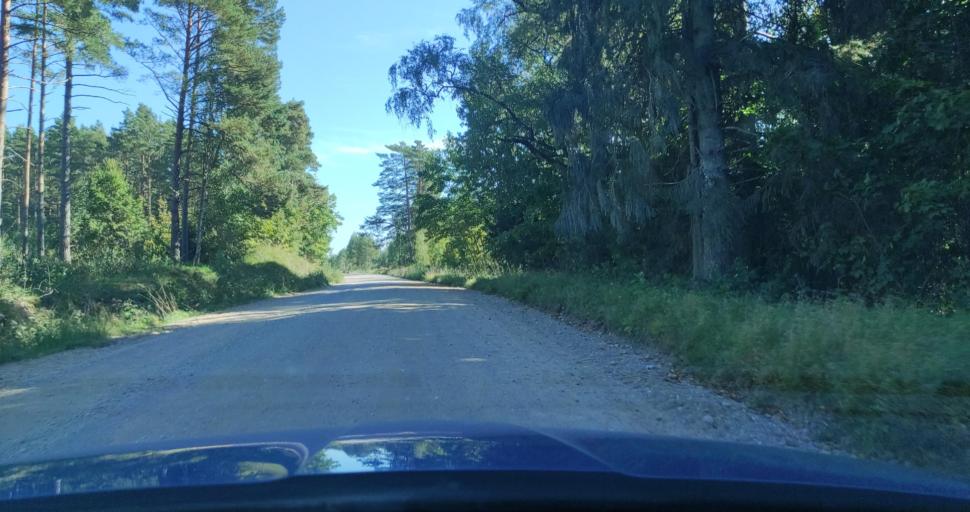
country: LV
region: Pavilostas
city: Pavilosta
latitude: 56.8392
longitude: 21.3764
